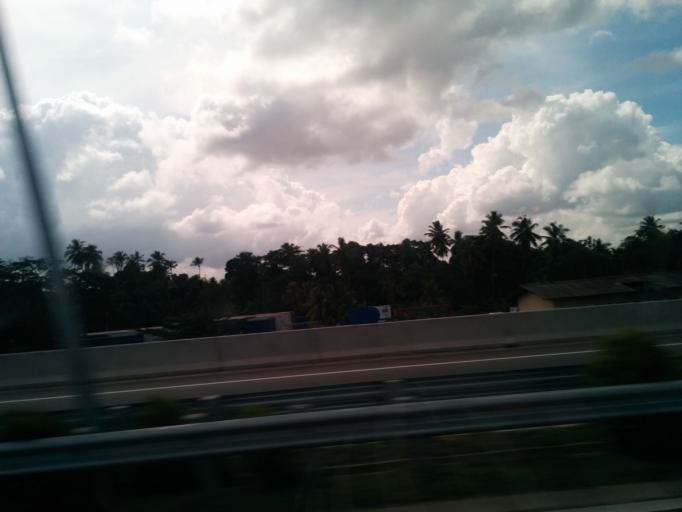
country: LK
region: Western
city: Wattala
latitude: 6.9834
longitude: 79.8992
